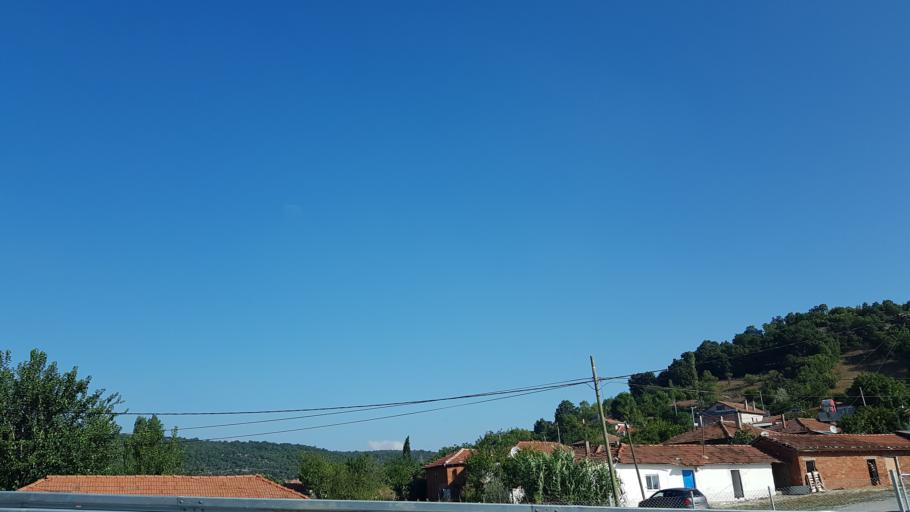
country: TR
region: Balikesir
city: Ertugrul
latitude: 39.5510
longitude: 27.6877
